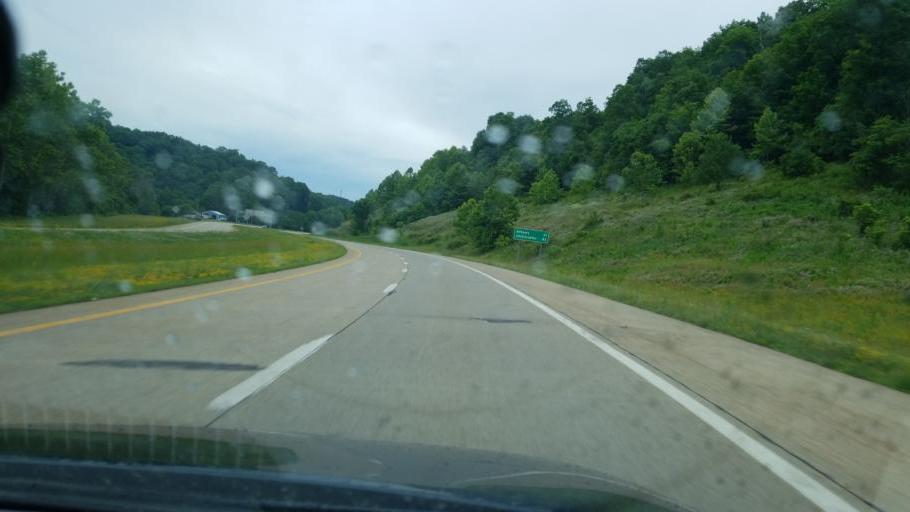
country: US
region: West Virginia
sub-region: Wood County
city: Washington
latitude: 39.2129
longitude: -81.8218
